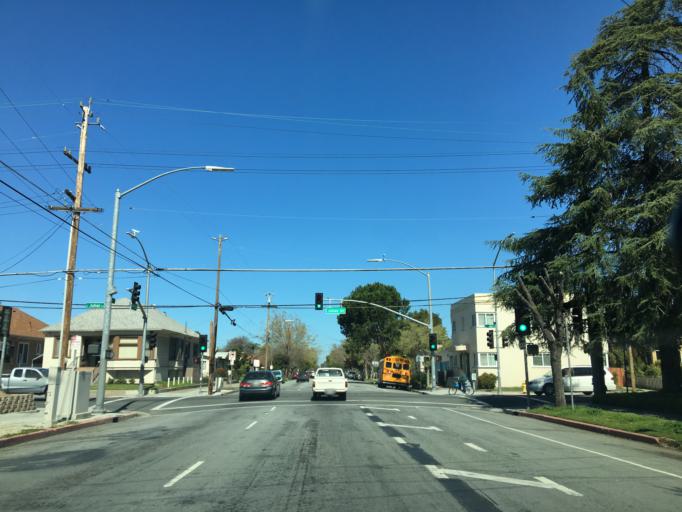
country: US
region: California
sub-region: Santa Clara County
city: San Jose
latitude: 37.3453
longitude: -121.8830
